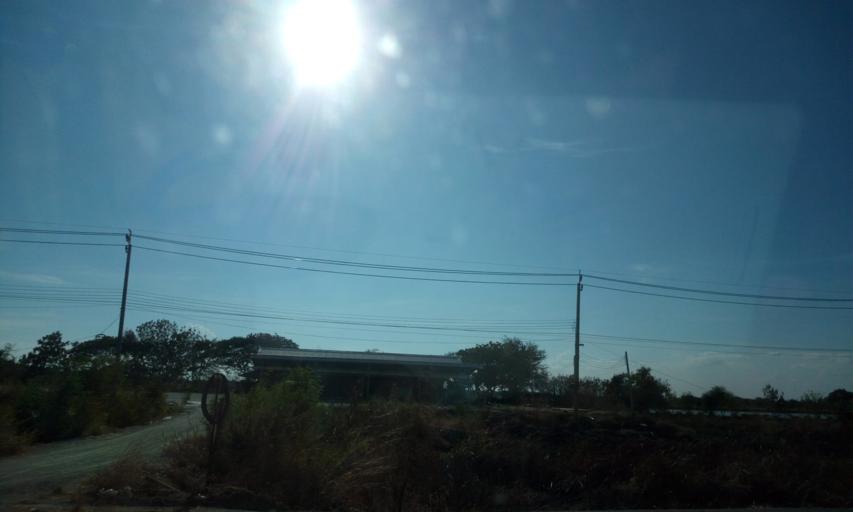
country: TH
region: Samut Prakan
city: Bang Bo District
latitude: 13.5444
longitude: 100.7512
